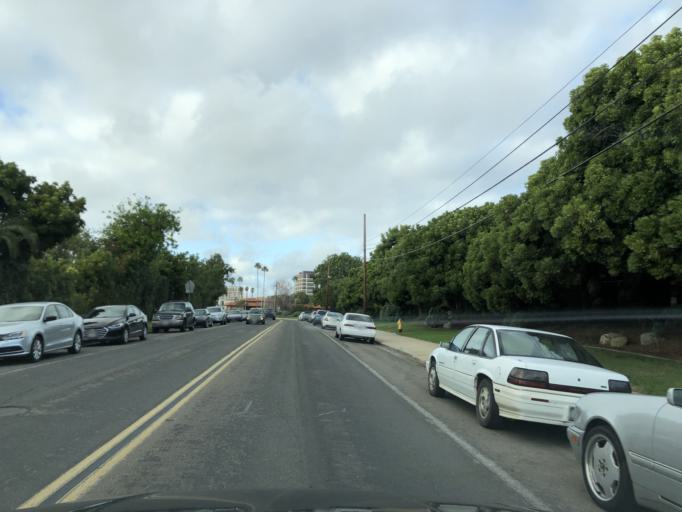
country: US
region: California
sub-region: San Diego County
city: La Jolla
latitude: 32.8147
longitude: -117.1821
